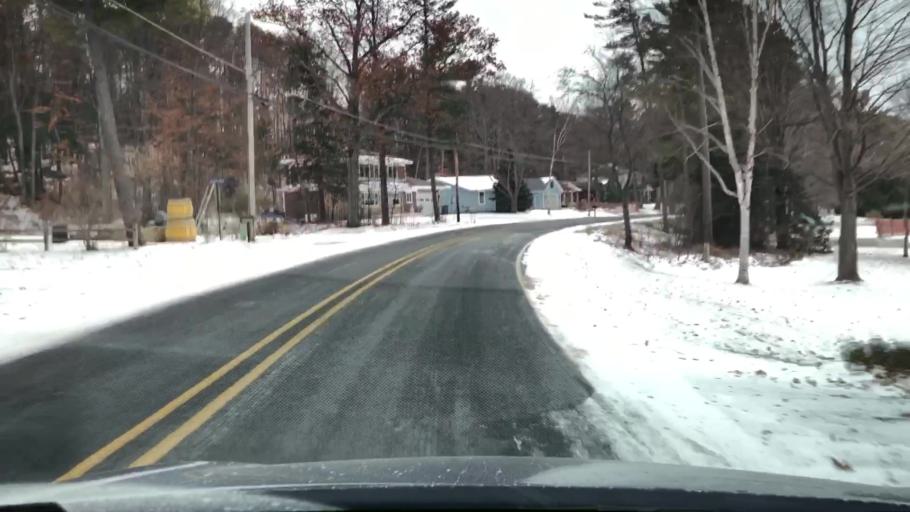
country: US
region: Michigan
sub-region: Grand Traverse County
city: Traverse City
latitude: 44.8269
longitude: -85.5664
